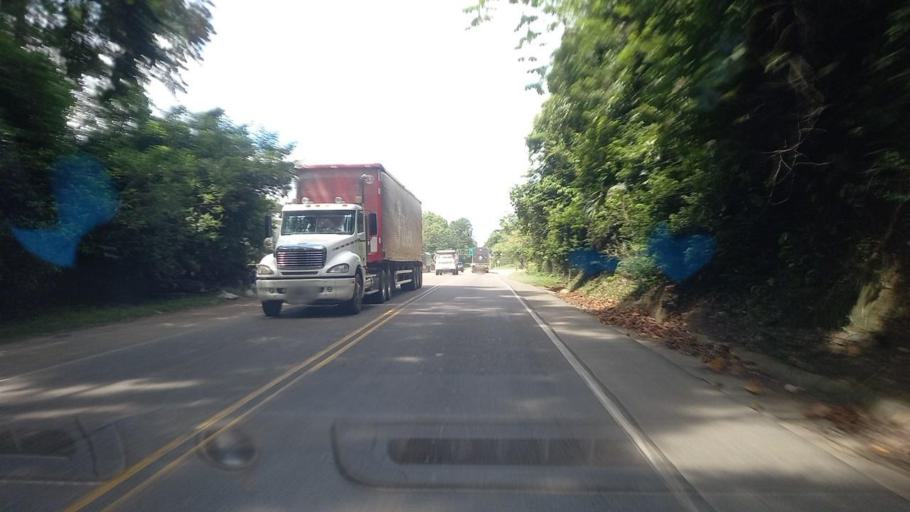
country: CO
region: Santander
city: Sabana de Torres
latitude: 7.1277
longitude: -73.5731
